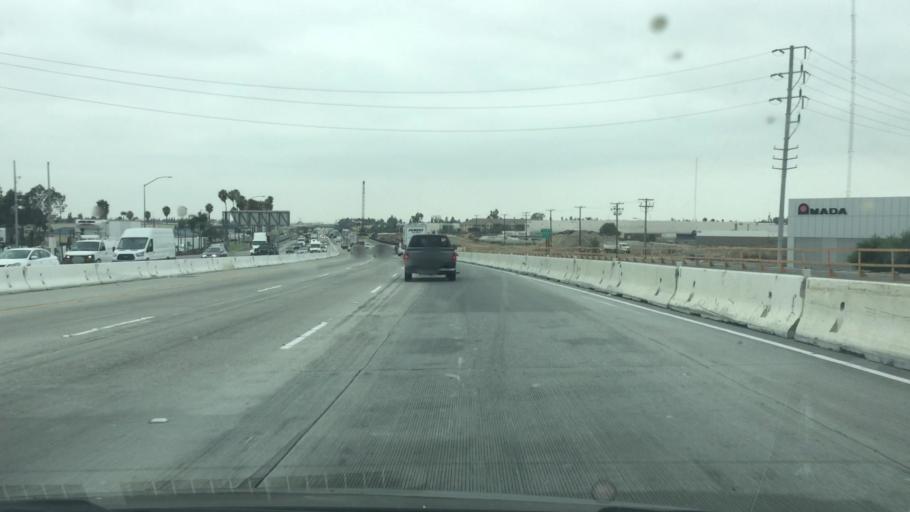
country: US
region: California
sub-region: Orange County
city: Buena Park
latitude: 33.8742
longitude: -118.0107
